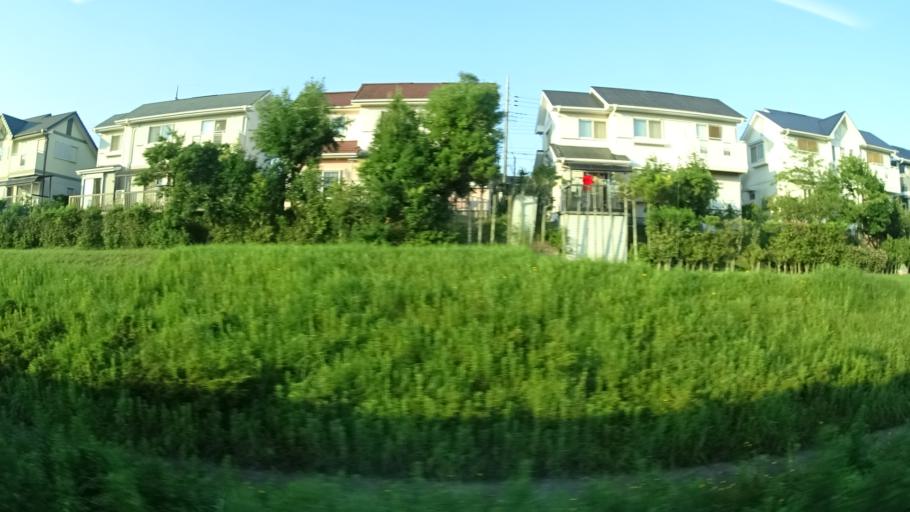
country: JP
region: Ibaraki
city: Ishioka
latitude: 36.1825
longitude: 140.2864
